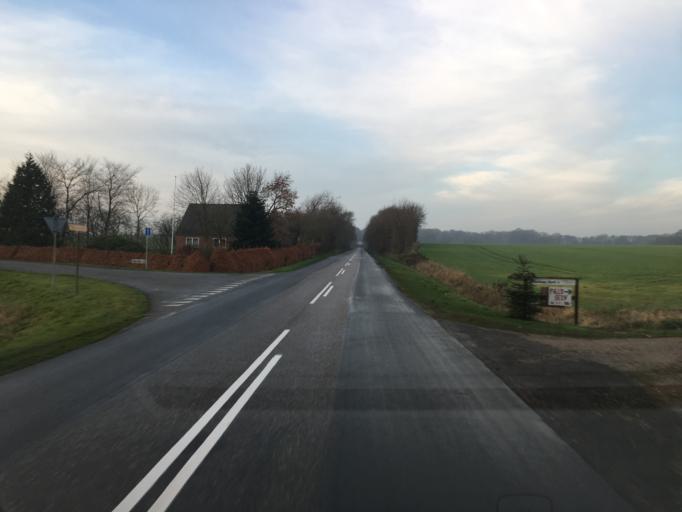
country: DK
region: South Denmark
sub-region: Tonder Kommune
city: Toftlund
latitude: 55.1376
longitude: 9.0593
